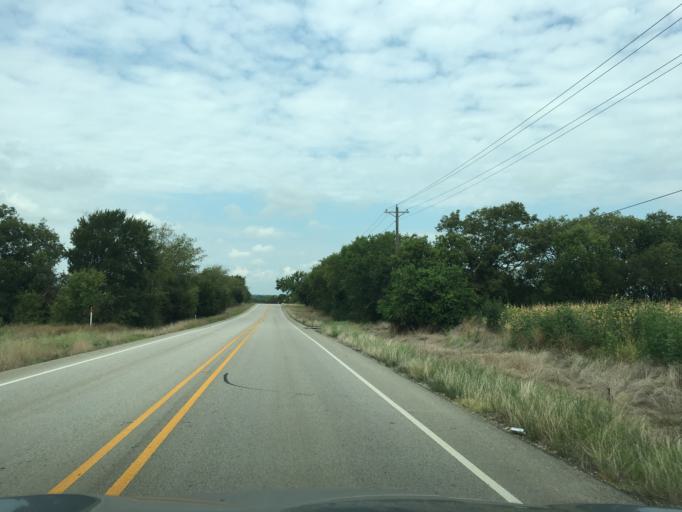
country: US
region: Texas
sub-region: Collin County
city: Anna
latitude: 33.3455
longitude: -96.6003
